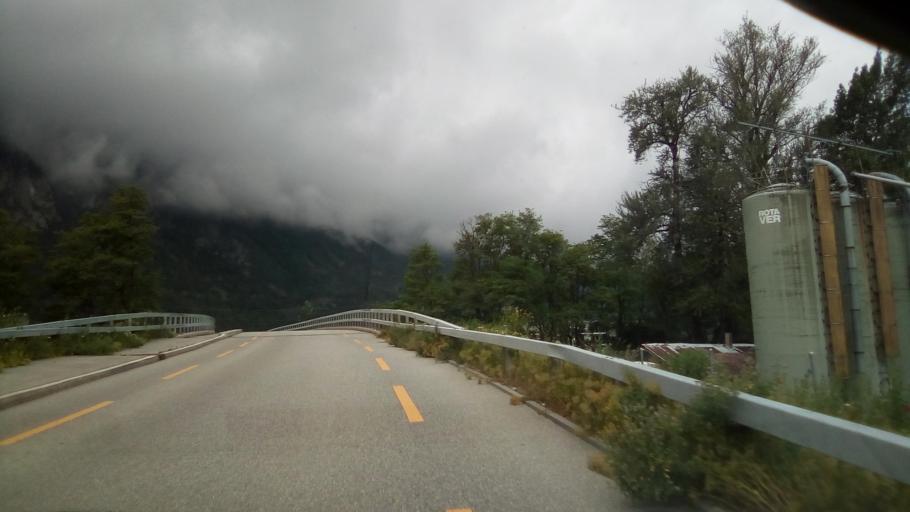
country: CH
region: Valais
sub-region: Martigny District
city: Martigny-Ville
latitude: 46.1145
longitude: 7.0702
